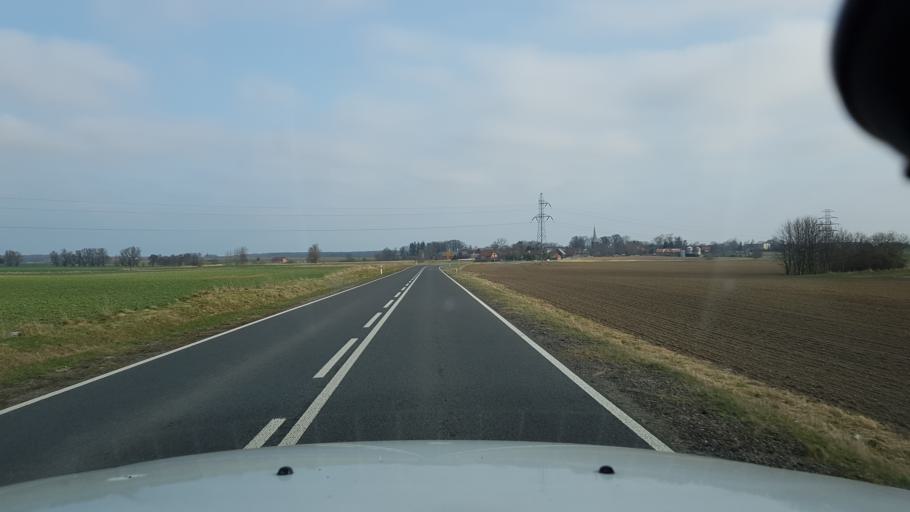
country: PL
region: West Pomeranian Voivodeship
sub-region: Powiat koszalinski
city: Sianow
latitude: 54.2871
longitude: 16.2713
